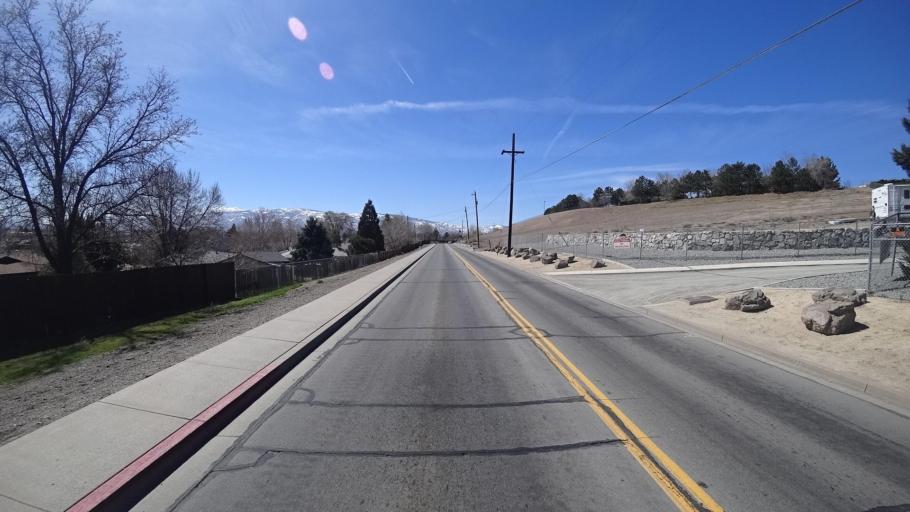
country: US
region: Nevada
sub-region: Washoe County
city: Sparks
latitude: 39.5523
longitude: -119.7815
